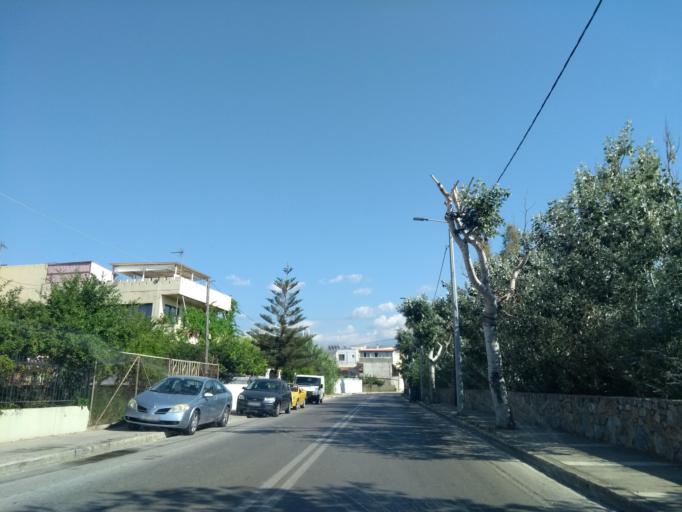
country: GR
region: Crete
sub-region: Nomos Chanias
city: Chania
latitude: 35.5109
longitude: 24.0021
